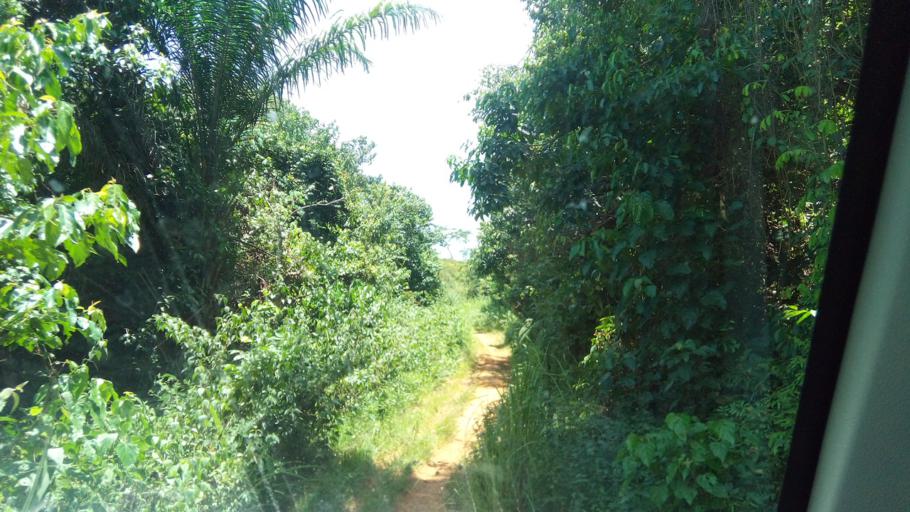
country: AO
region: Zaire
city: Mbanza Congo
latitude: -5.8051
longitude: 14.2431
